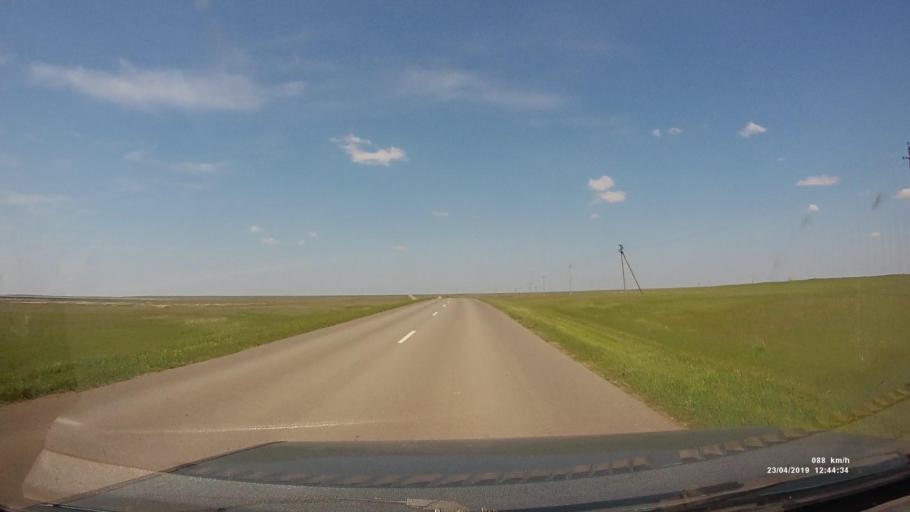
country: RU
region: Kalmykiya
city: Yashalta
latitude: 46.4786
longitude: 42.6467
